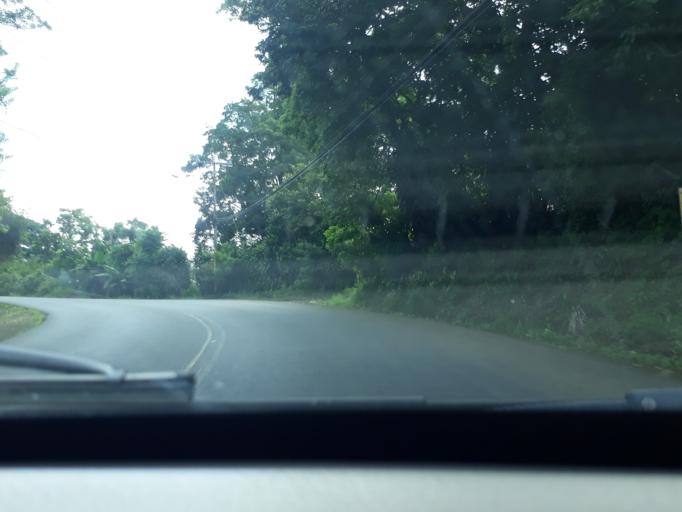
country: CR
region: Alajuela
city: Naranjo
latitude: 10.0394
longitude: -84.3471
